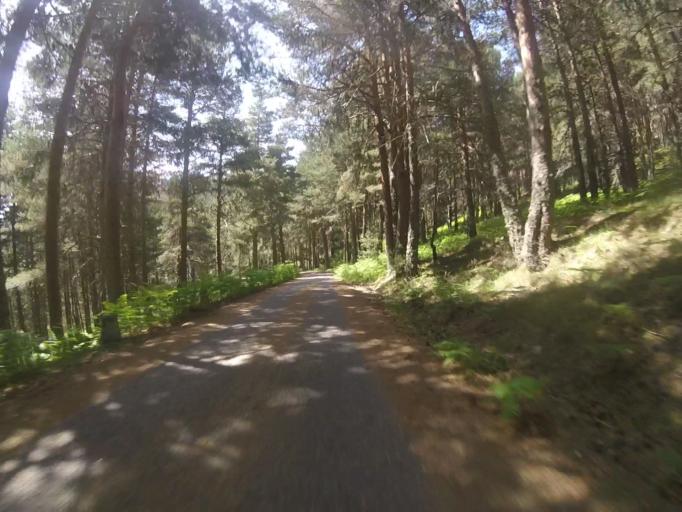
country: ES
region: Madrid
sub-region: Provincia de Madrid
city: Cercedilla
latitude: 40.8108
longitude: -4.0552
